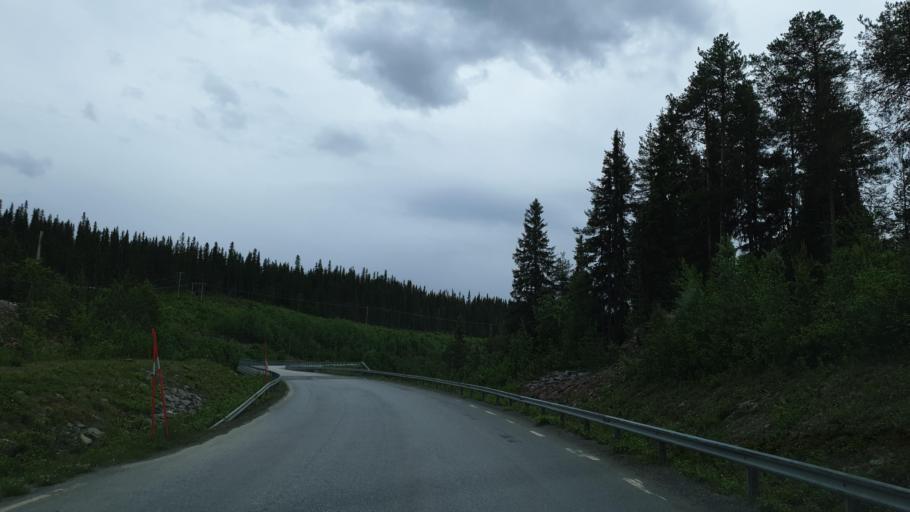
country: SE
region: Vaesterbotten
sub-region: Storumans Kommun
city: Fristad
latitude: 65.4251
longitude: 16.1713
